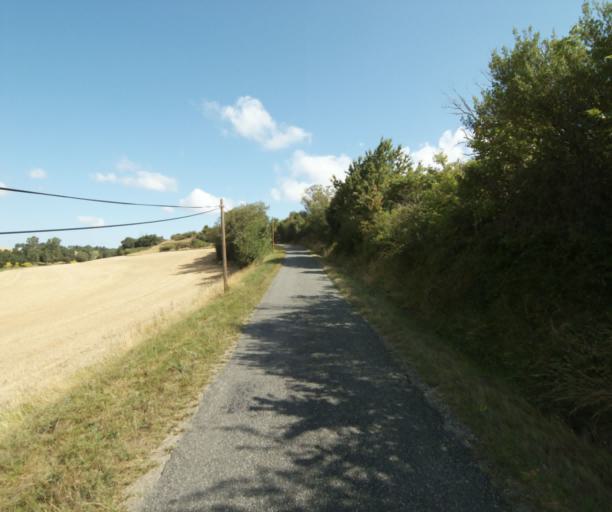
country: FR
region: Midi-Pyrenees
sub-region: Departement de la Haute-Garonne
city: Saint-Felix-Lauragais
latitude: 43.4501
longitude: 1.8284
